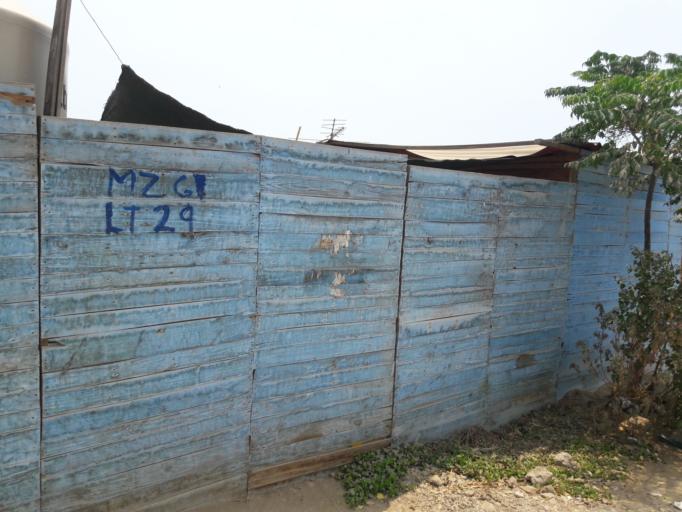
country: PE
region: Lima
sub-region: Lima
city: Santa Rosa
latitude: -11.7700
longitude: -77.1631
